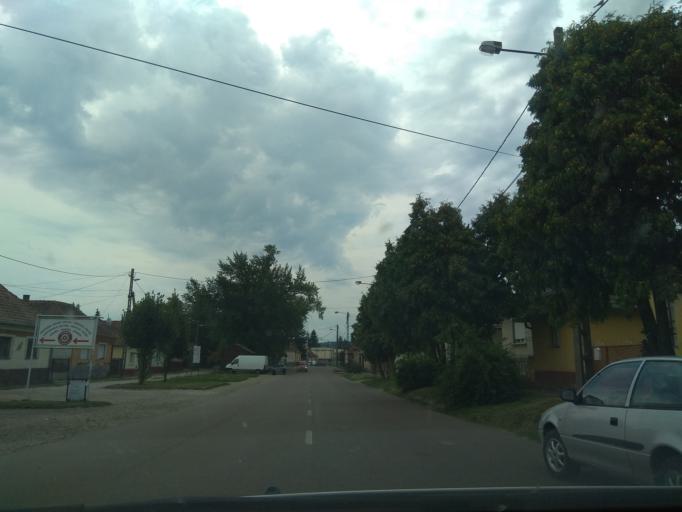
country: HU
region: Heves
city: Petervasara
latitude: 48.0202
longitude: 20.1023
